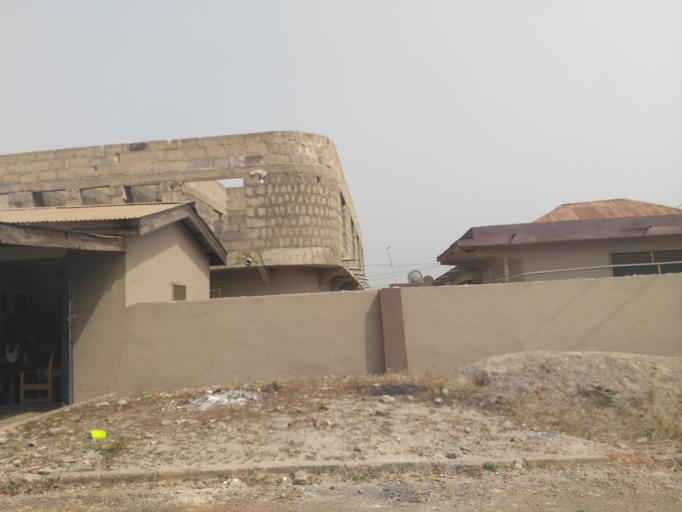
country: GH
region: Ashanti
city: Kumasi
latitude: 6.6812
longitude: -1.5978
